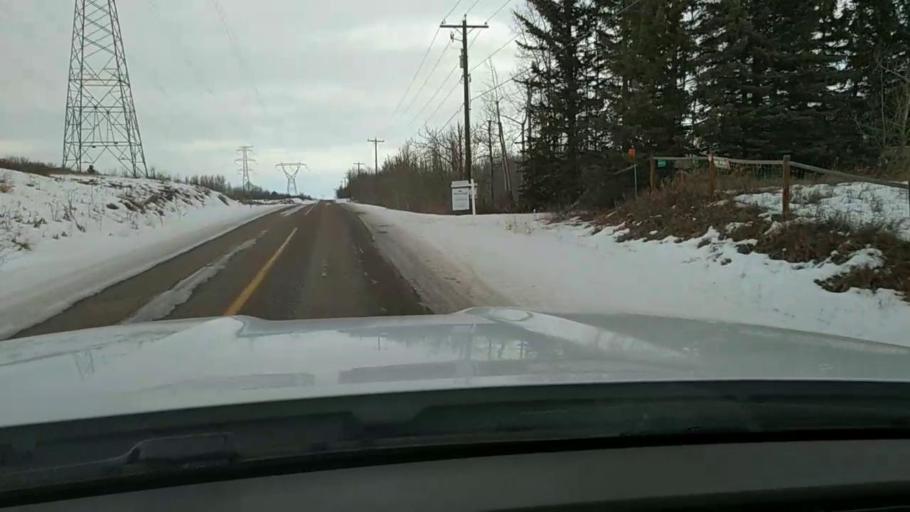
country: CA
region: Alberta
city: Cochrane
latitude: 51.1770
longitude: -114.2575
